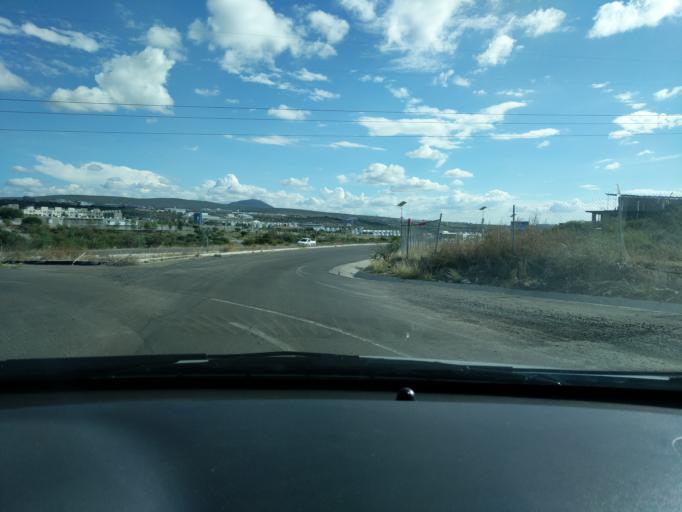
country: MX
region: Queretaro
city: La Canada
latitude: 20.5932
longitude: -100.3211
